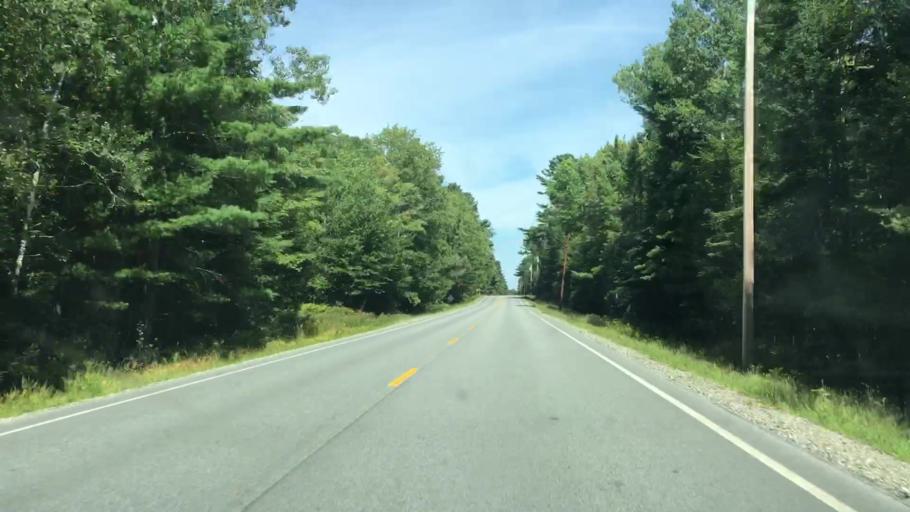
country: US
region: Maine
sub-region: Penobscot County
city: Howland
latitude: 45.2166
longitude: -68.7923
